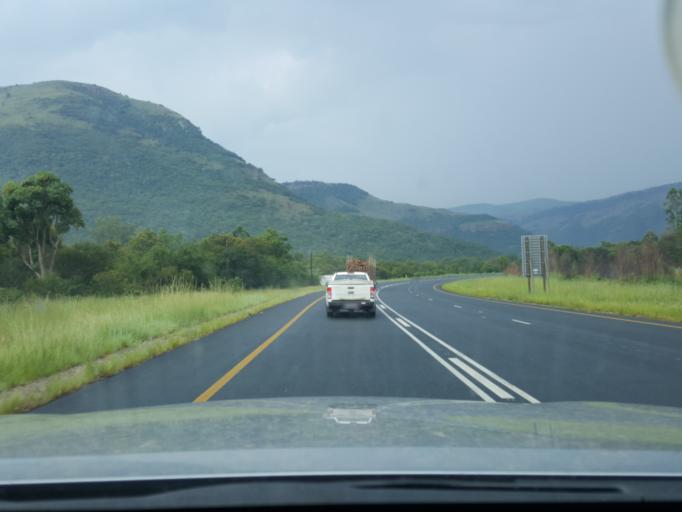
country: ZA
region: Mpumalanga
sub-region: Nkangala District Municipality
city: Belfast
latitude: -25.6373
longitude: 30.3935
